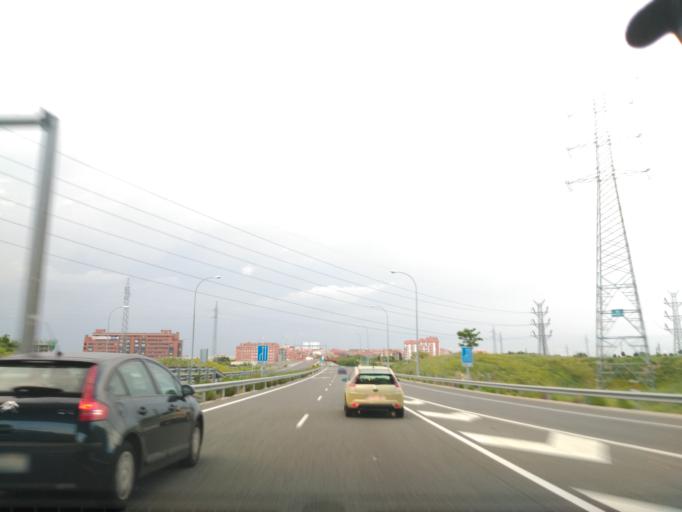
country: ES
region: Madrid
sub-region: Provincia de Madrid
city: Villaverde
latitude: 40.3366
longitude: -3.6717
